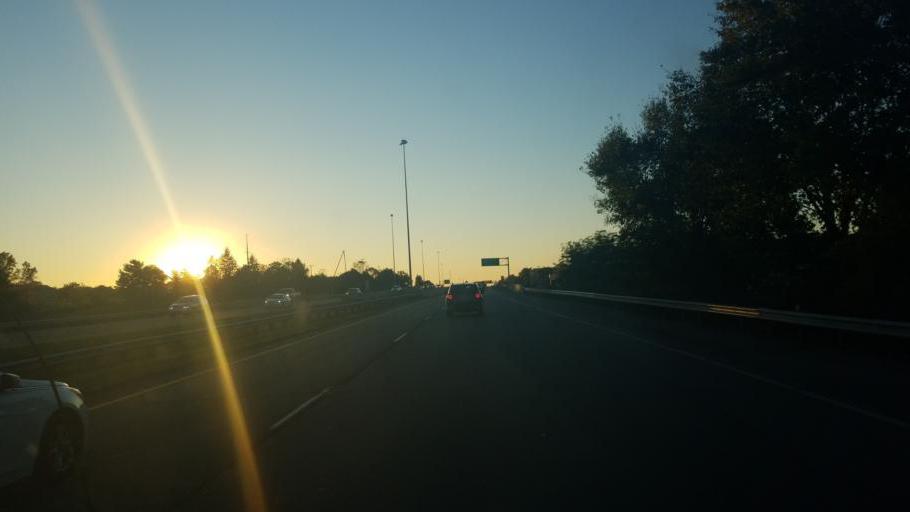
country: US
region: Ohio
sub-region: Stark County
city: Canton
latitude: 40.8290
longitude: -81.3710
